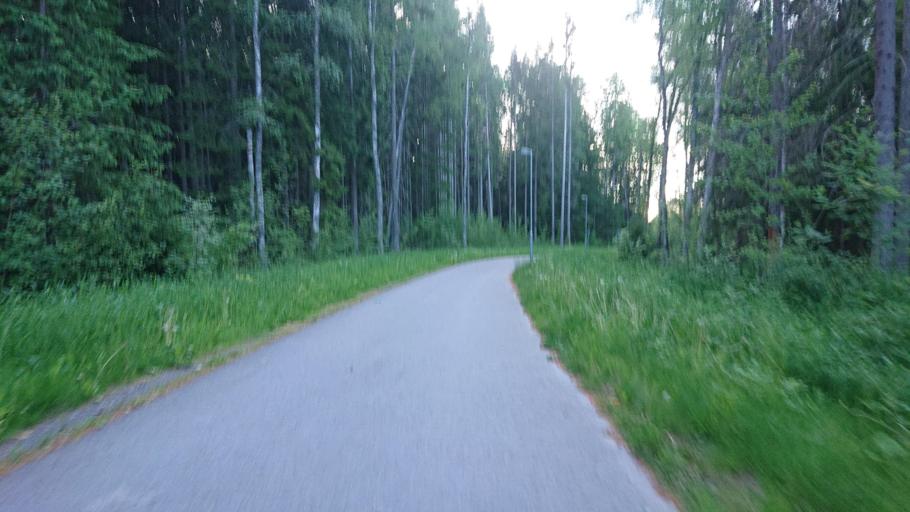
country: SE
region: Stockholm
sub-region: Osterakers Kommun
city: Akersberga
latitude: 59.4917
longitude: 18.3129
